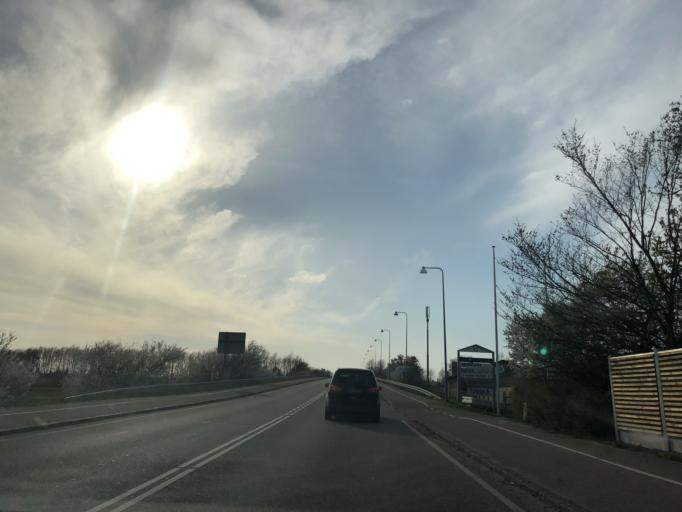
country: DK
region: Zealand
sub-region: Koge Kommune
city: Koge
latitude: 55.4482
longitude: 12.1881
